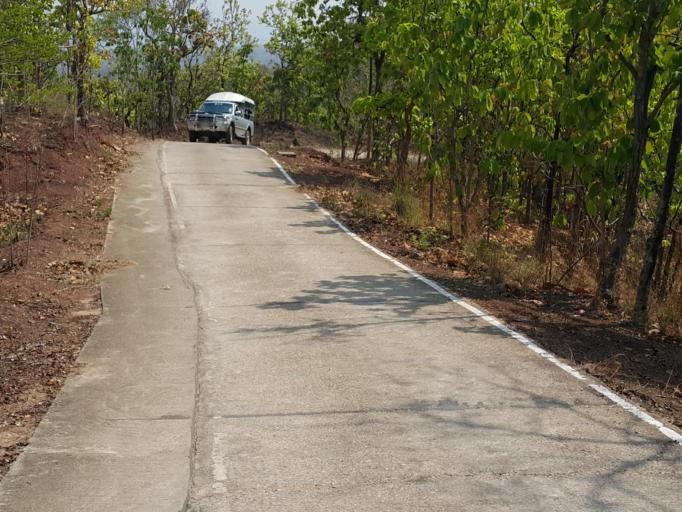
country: TH
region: Lampang
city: Chae Hom
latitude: 18.7465
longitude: 99.5412
